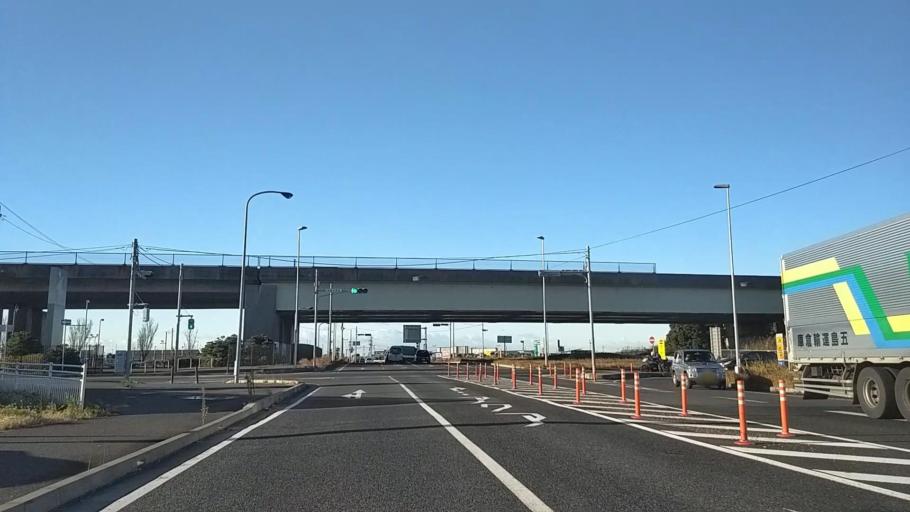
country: JP
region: Chiba
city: Kisarazu
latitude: 35.4342
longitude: 139.9226
